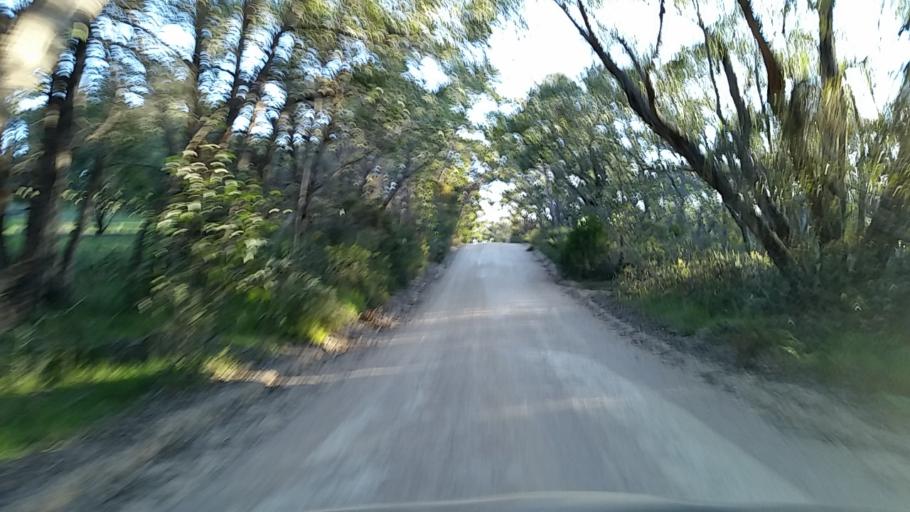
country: AU
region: South Australia
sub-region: Alexandrina
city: Mount Compass
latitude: -35.3020
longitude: 138.6792
